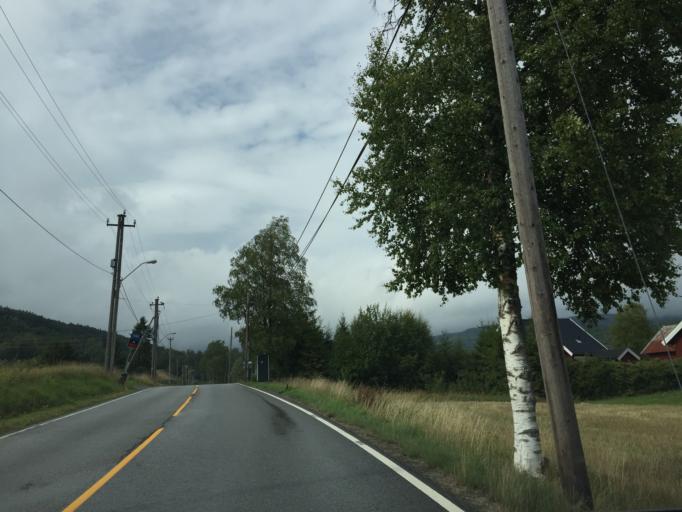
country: NO
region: Akershus
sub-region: Baerum
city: Lysaker
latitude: 60.0179
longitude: 10.5964
